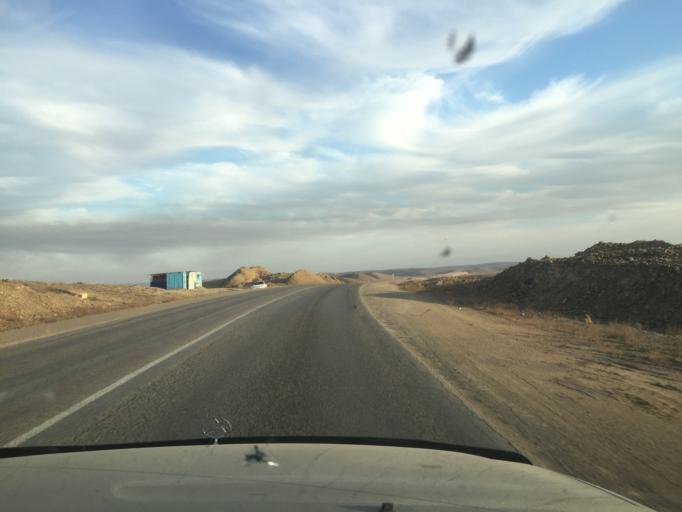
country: KZ
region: Almaty Oblysy
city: Ulken
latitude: 45.0757
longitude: 73.9835
